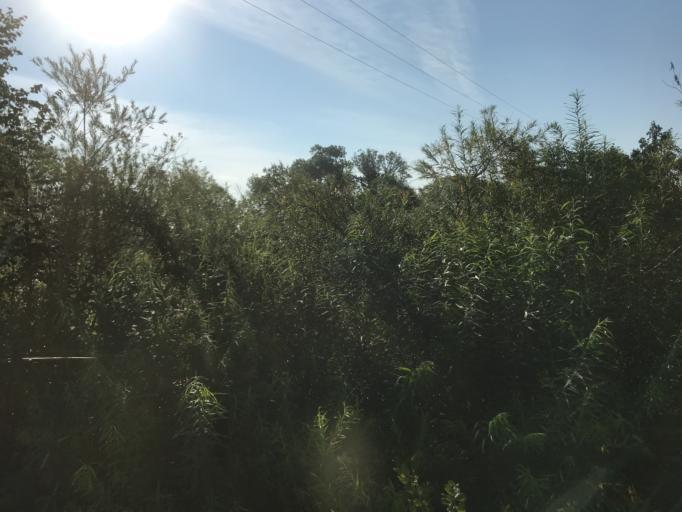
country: CZ
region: Jihocesky
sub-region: Okres Jindrichuv Hradec
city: Lomnice nad Luznici
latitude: 49.0872
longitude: 14.7282
